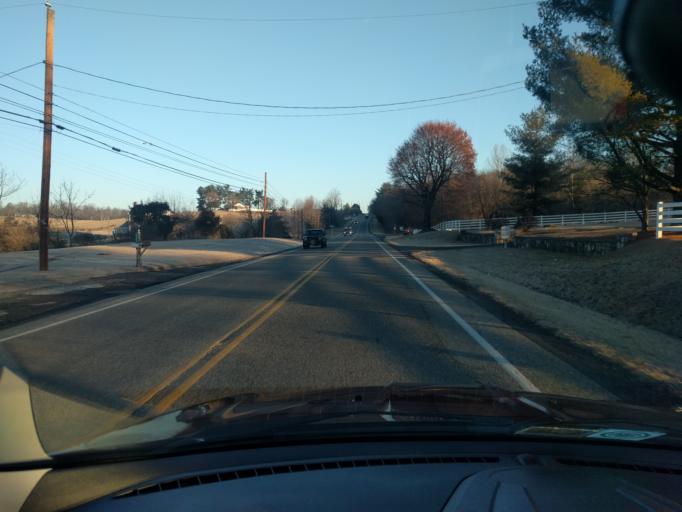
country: US
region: Virginia
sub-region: Augusta County
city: Weyers Cave
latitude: 38.3086
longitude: -78.9356
